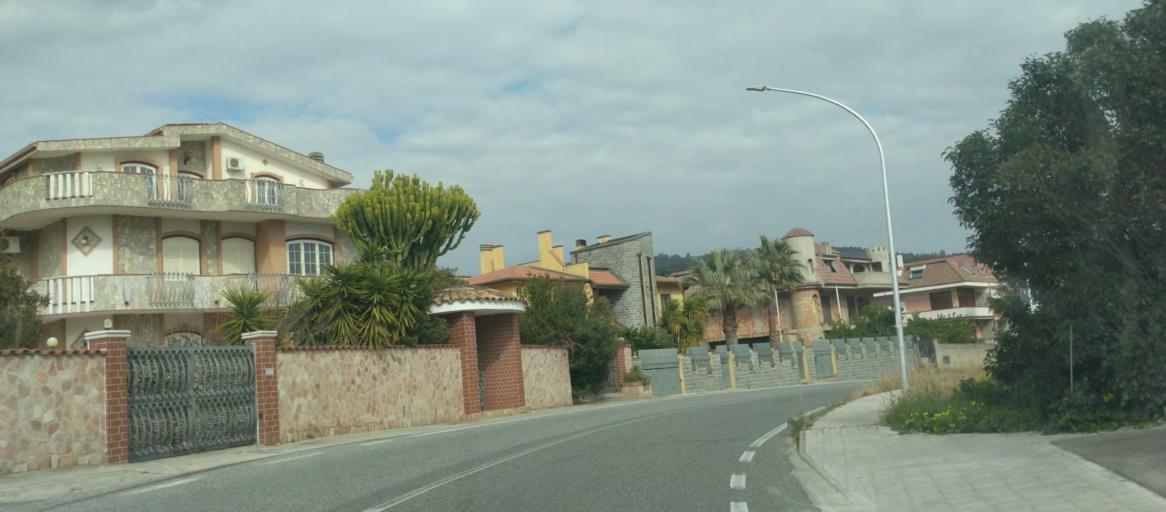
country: IT
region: Calabria
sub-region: Provincia di Catanzaro
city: Montepaone Lido
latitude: 38.7295
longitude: 16.5347
